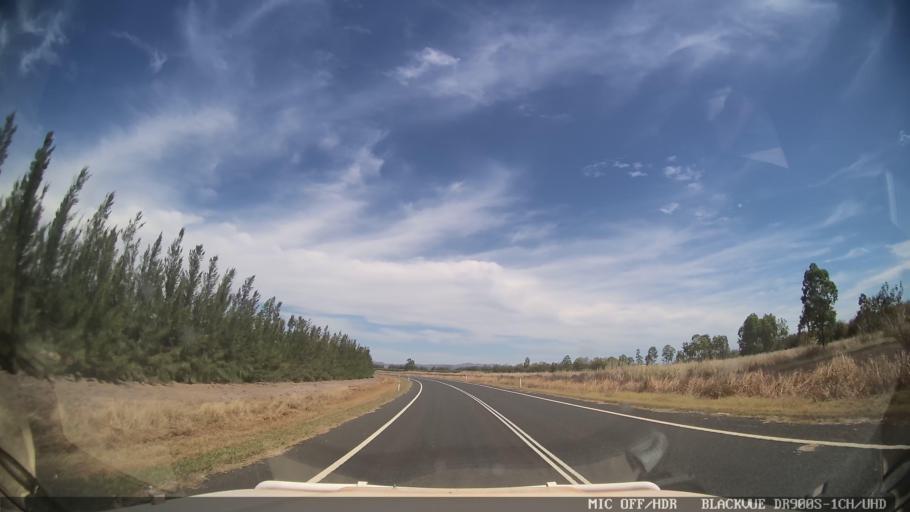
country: AU
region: Queensland
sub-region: Cook
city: Cooktown
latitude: -15.8327
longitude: 144.8568
